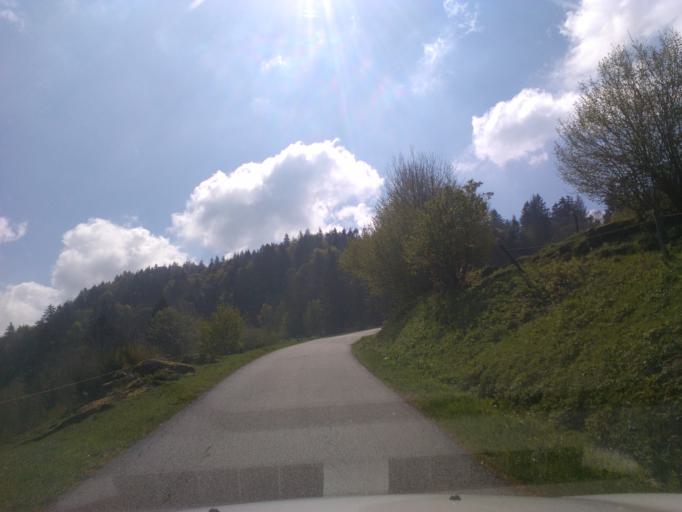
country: FR
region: Lorraine
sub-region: Departement des Vosges
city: Cornimont
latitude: 47.9850
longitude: 6.7978
